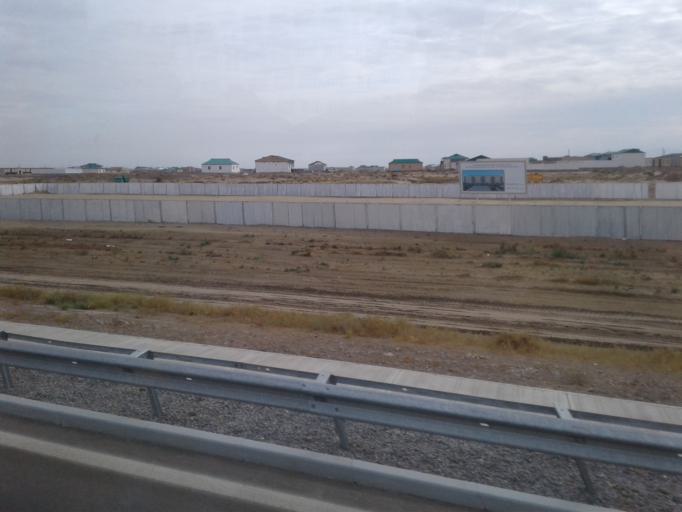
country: TM
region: Lebap
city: Turkmenabat
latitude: 38.9806
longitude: 63.5546
